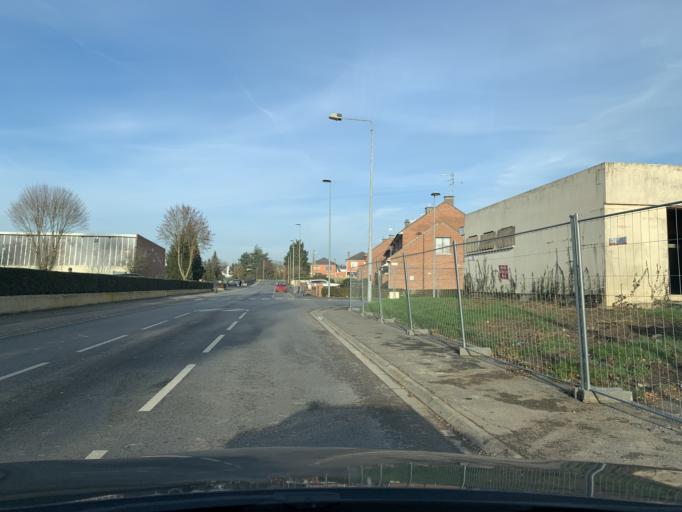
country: FR
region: Nord-Pas-de-Calais
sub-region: Departement du Nord
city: Cambrai
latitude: 50.1620
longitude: 3.2579
